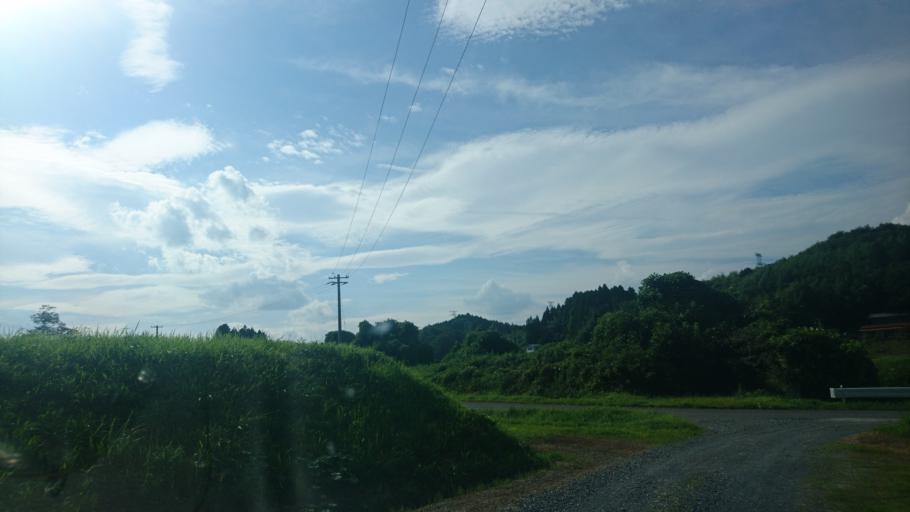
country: JP
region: Miyagi
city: Furukawa
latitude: 38.7670
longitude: 140.9523
